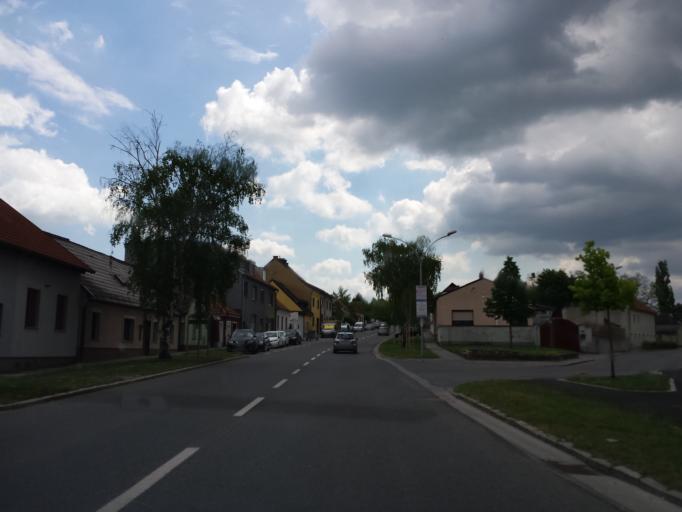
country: AT
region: Lower Austria
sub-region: Politischer Bezirk Wien-Umgebung
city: Fischamend Dorf
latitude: 48.1191
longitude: 16.6160
